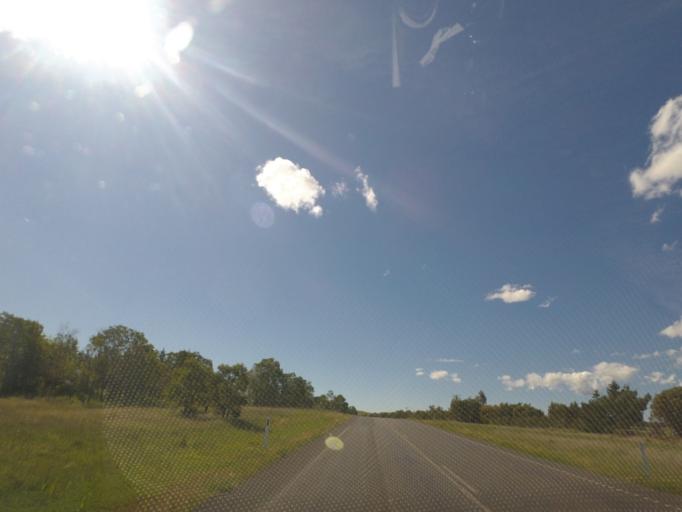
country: AU
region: Victoria
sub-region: Moorabool
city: Bacchus Marsh
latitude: -37.6486
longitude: 144.2284
